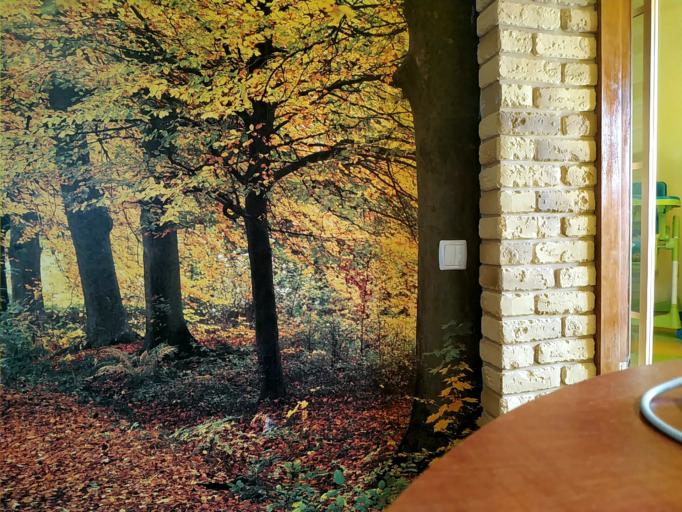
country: RU
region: Tverskaya
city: Kalashnikovo
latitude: 57.3346
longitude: 35.3287
